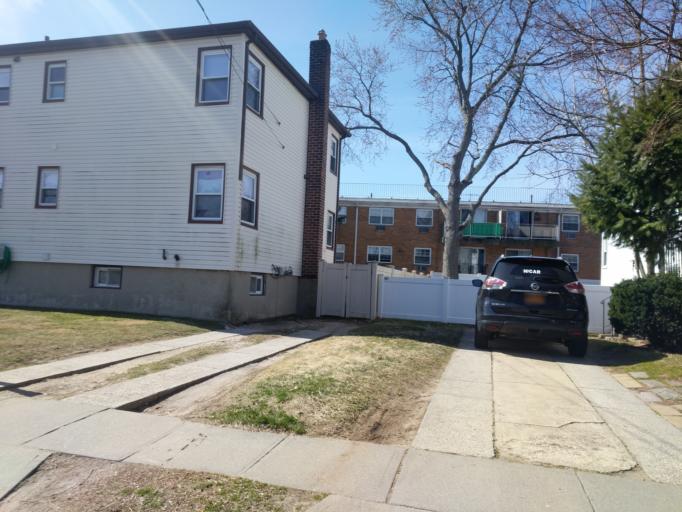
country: US
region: New York
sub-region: Nassau County
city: Lynbrook
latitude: 40.6506
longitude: -73.6754
